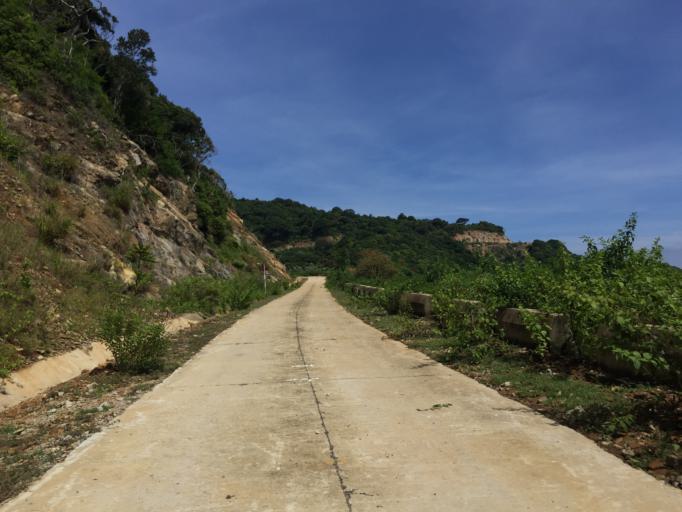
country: VN
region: Quang Nam
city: Hoi An
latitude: 15.9688
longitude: 108.5078
